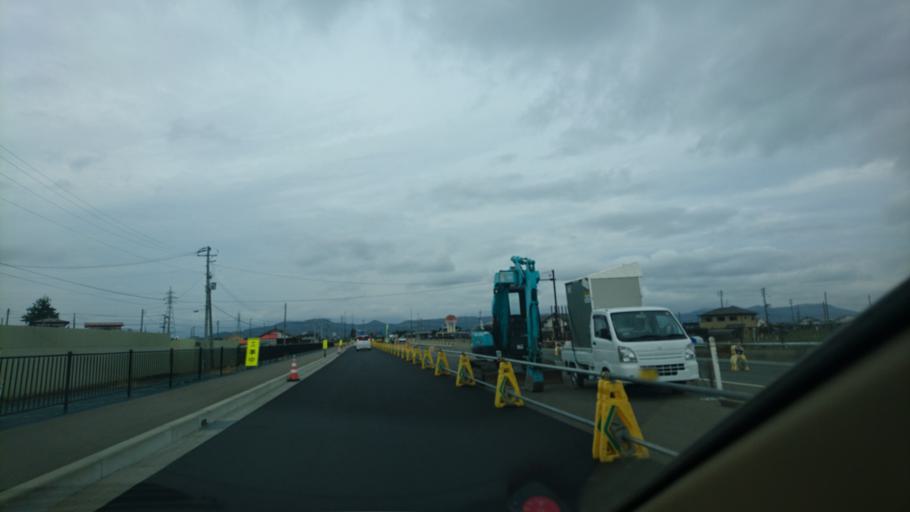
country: JP
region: Iwate
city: Morioka-shi
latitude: 39.6888
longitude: 141.1139
